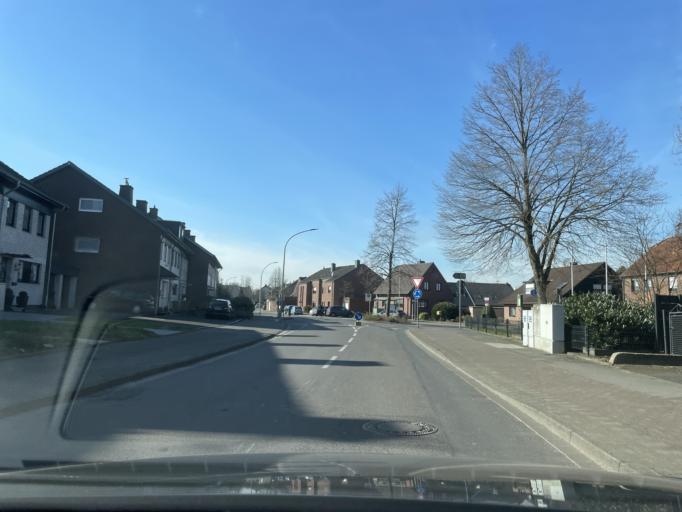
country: DE
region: North Rhine-Westphalia
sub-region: Regierungsbezirk Dusseldorf
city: Viersen
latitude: 51.2061
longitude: 6.3730
